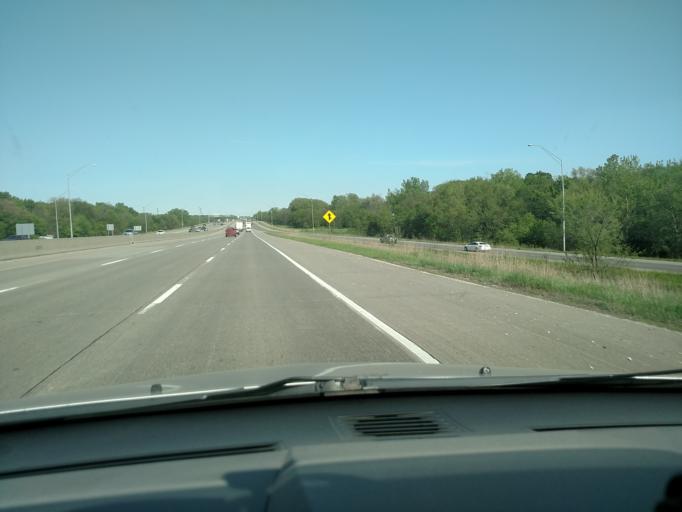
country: US
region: Iowa
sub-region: Polk County
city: Johnston
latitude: 41.6519
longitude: -93.6959
